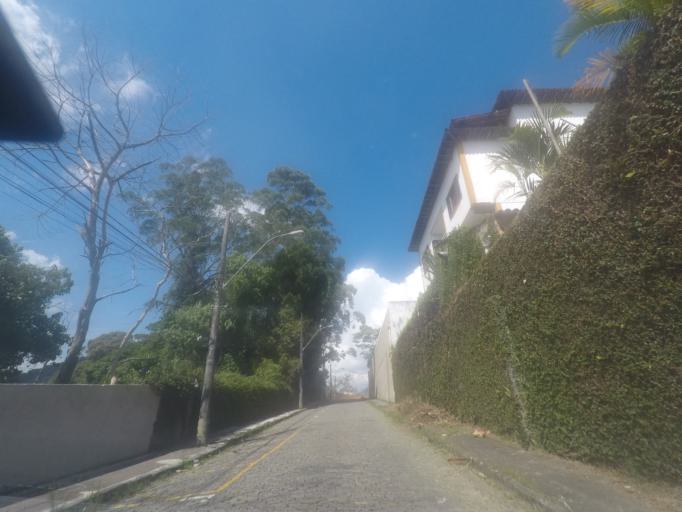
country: BR
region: Rio de Janeiro
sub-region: Petropolis
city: Petropolis
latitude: -22.5088
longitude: -43.1796
